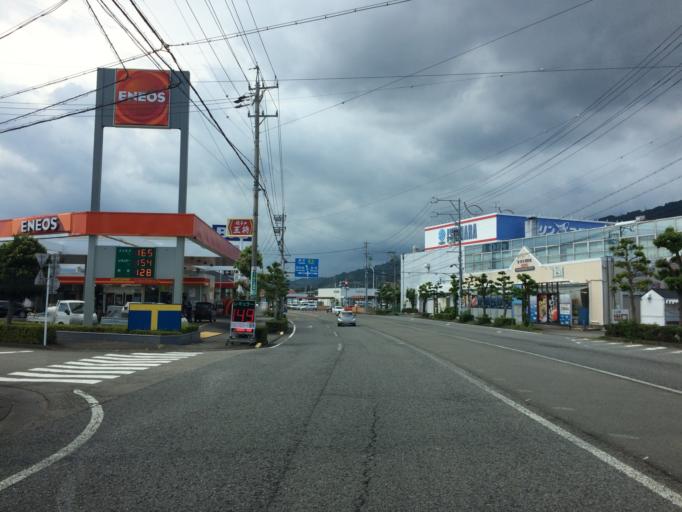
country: JP
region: Shizuoka
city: Yaizu
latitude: 34.8778
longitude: 138.3115
